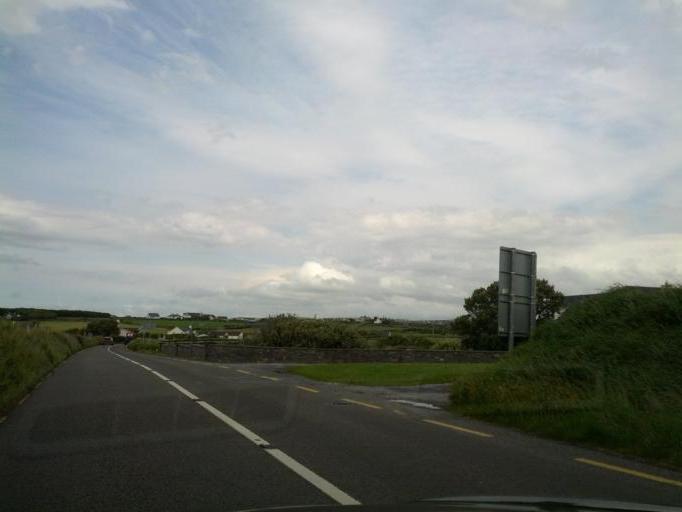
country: IE
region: Munster
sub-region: An Clar
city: Kilrush
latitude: 52.8402
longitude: -9.4269
